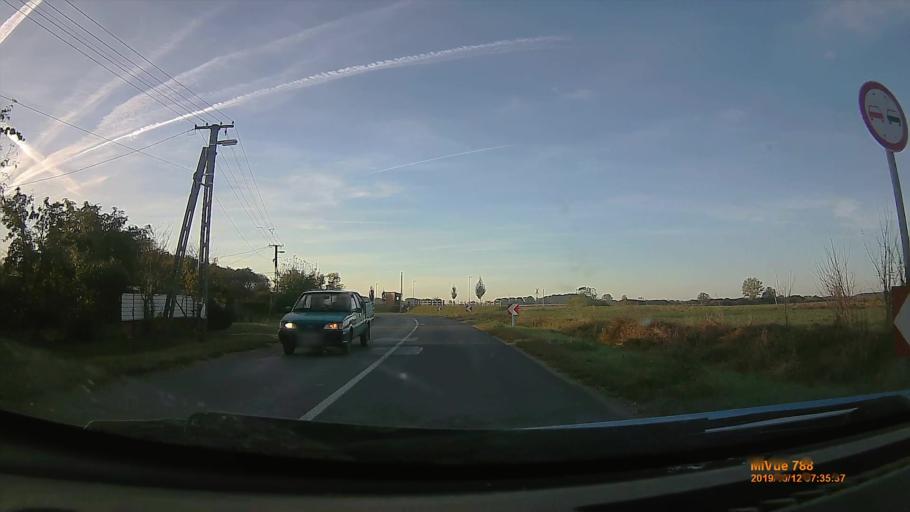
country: HU
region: Hajdu-Bihar
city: Pocsaj
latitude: 47.2522
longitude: 21.8107
